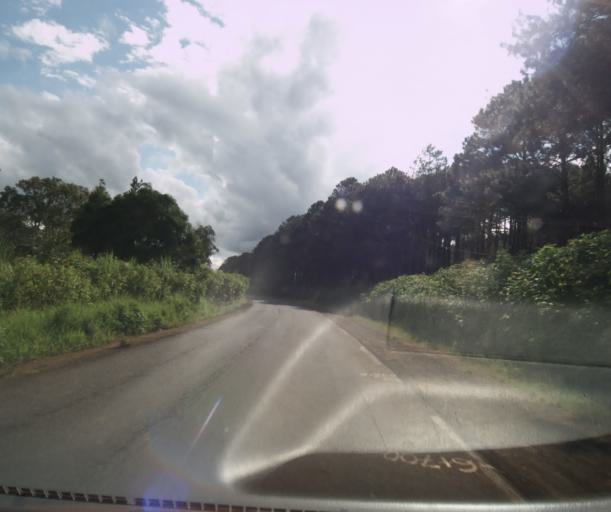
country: CM
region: West
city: Foumban
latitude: 5.6985
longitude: 10.8160
